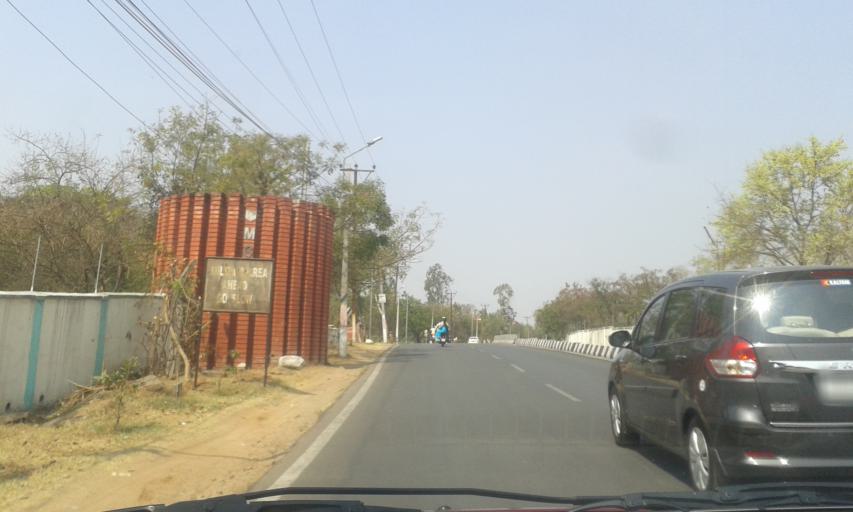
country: IN
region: Telangana
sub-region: Hyderabad
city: Malkajgiri
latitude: 17.4812
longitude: 78.5111
